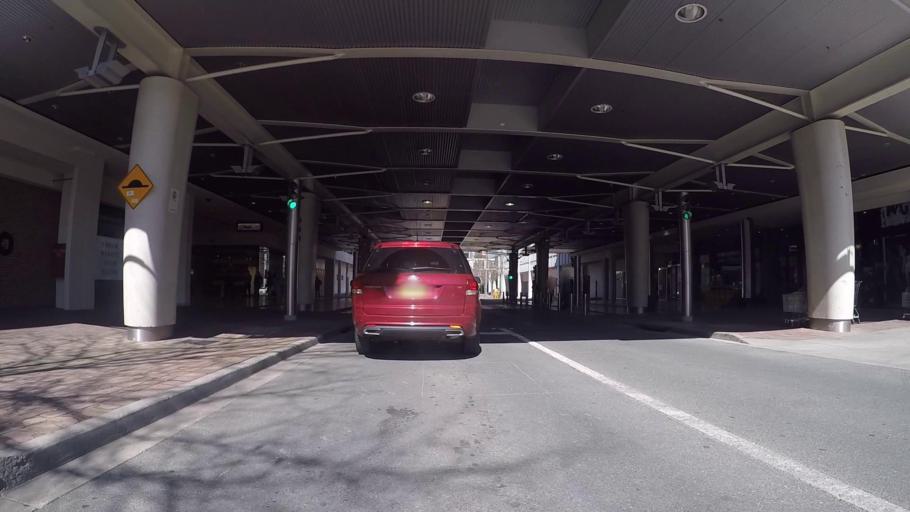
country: AU
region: Australian Capital Territory
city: Canberra
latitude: -35.2797
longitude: 149.1337
